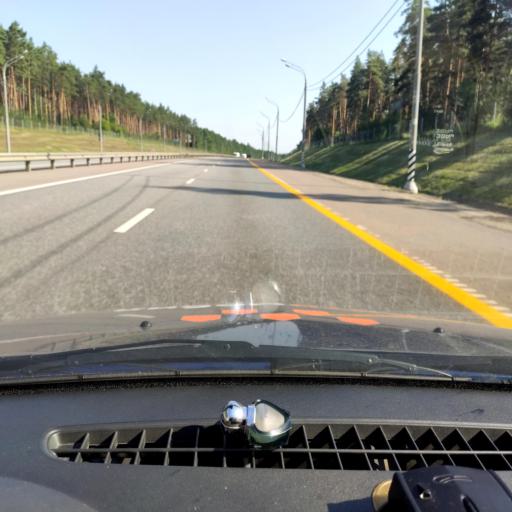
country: RU
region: Lipetsk
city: Khlevnoye
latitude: 52.3079
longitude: 39.0484
